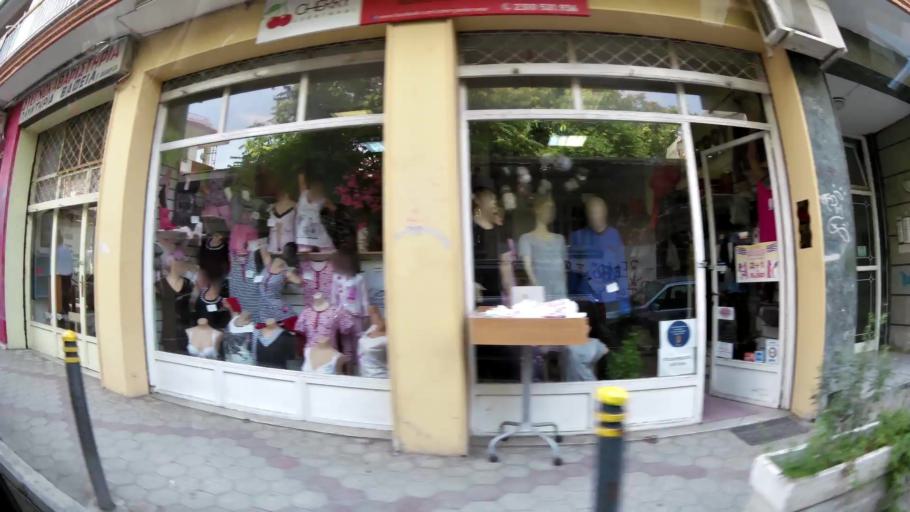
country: GR
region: Central Macedonia
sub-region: Nomos Thessalonikis
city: Sykies
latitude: 40.6487
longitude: 22.9513
